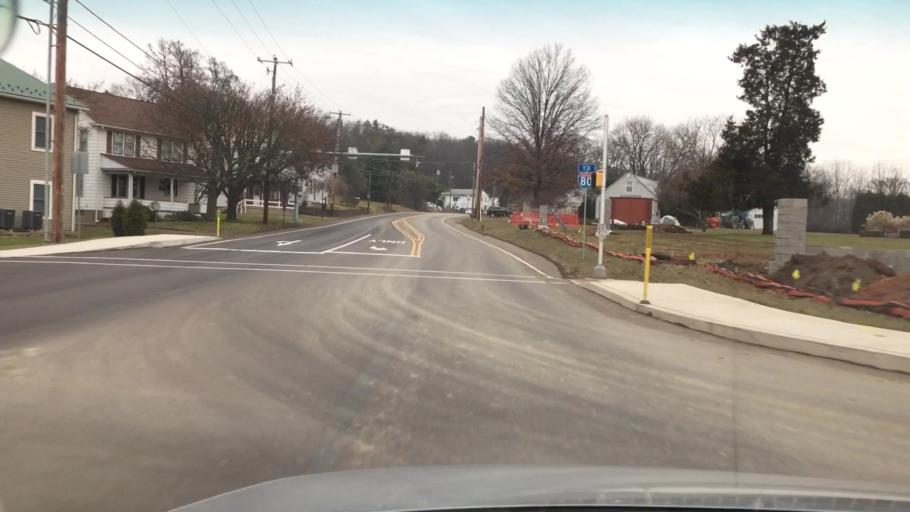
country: US
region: Pennsylvania
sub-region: Columbia County
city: Bloomsburg
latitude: 41.0120
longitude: -76.4440
